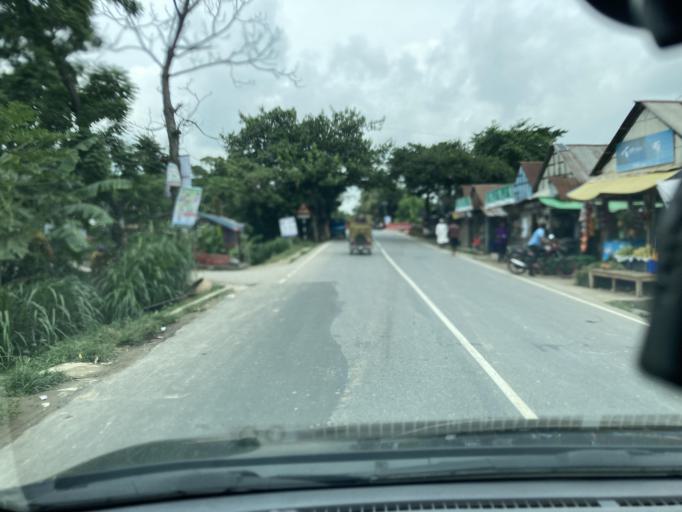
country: BD
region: Dhaka
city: Azimpur
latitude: 23.8058
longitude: 90.2081
